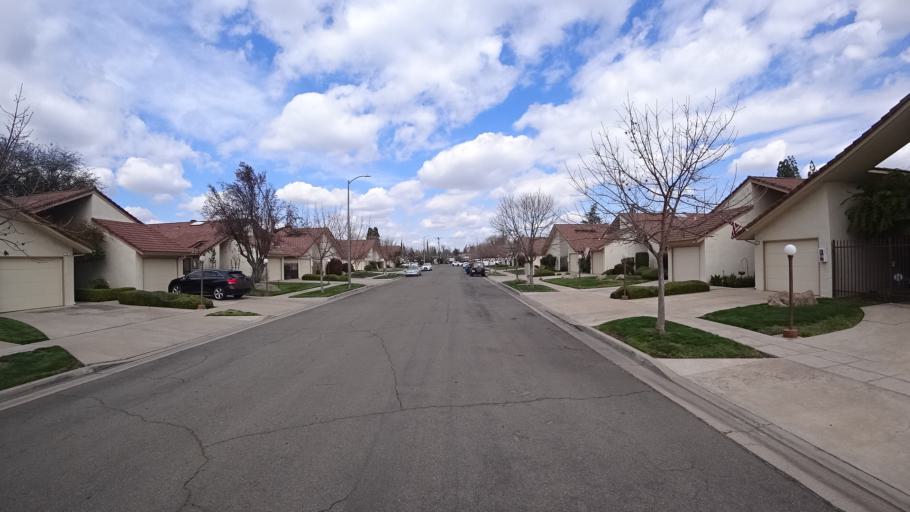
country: US
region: California
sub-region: Fresno County
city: Fresno
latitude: 36.8214
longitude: -119.8426
